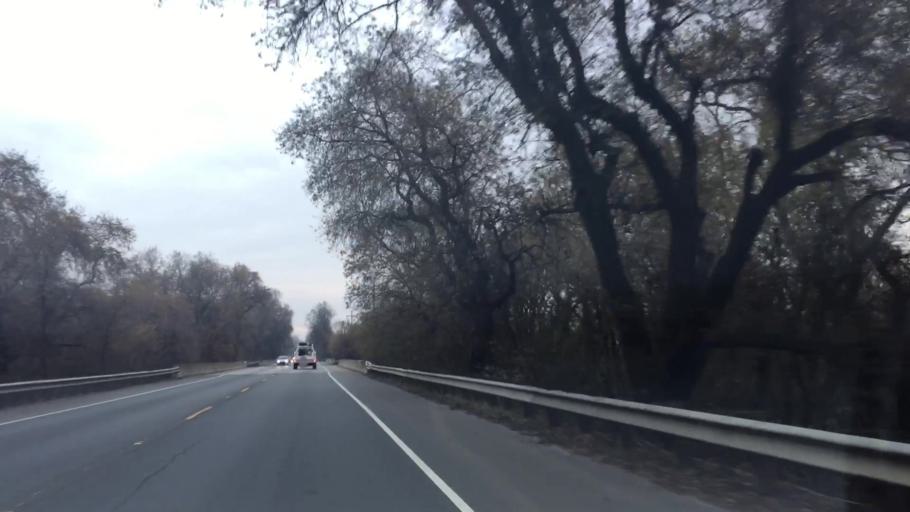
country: US
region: California
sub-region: Sutter County
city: Live Oak
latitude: 39.3076
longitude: -121.5954
